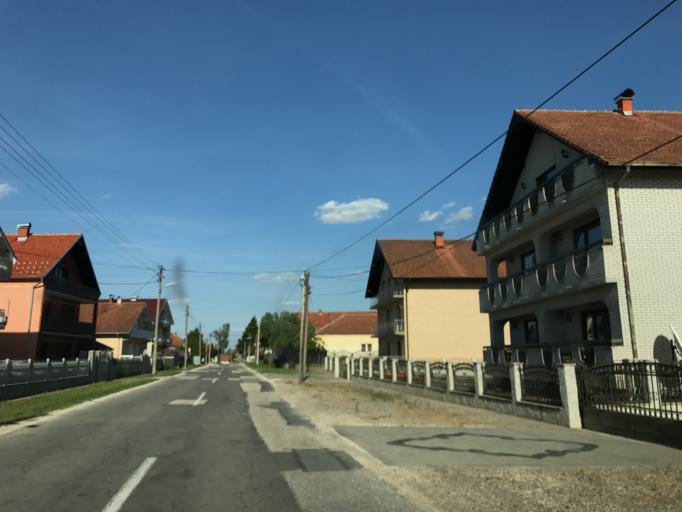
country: RO
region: Mehedinti
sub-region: Comuna Burila Mare
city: Burila Mare
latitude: 44.4916
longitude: 22.4831
